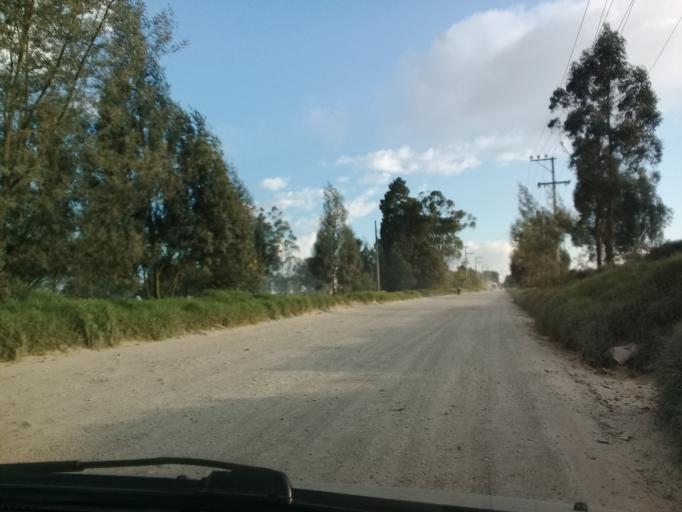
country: CO
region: Cundinamarca
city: Madrid
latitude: 4.7816
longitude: -74.2690
